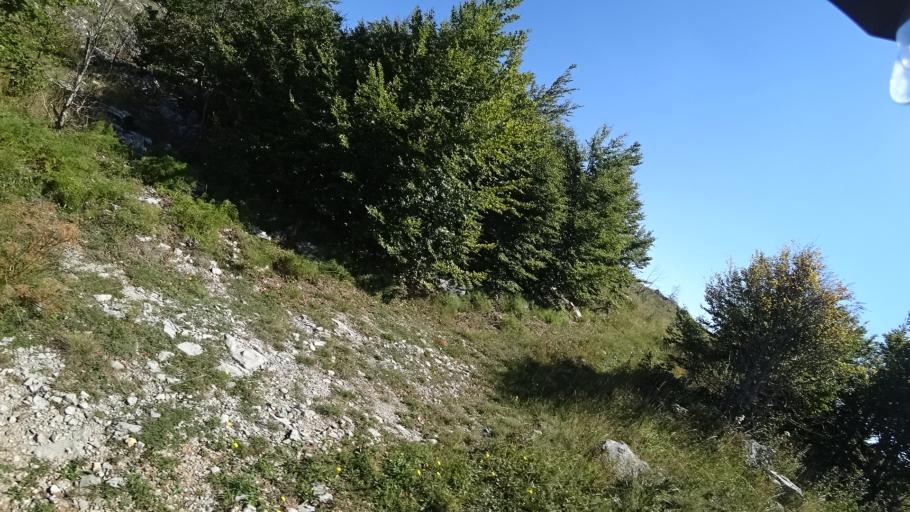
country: HR
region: Splitsko-Dalmatinska
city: Hrvace
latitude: 43.9145
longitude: 16.6105
